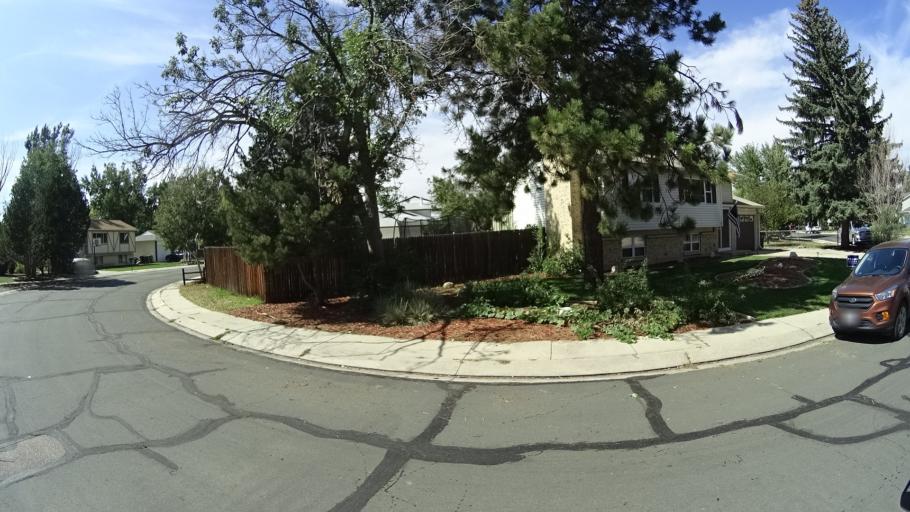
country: US
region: Colorado
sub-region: El Paso County
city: Cimarron Hills
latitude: 38.8990
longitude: -104.7538
